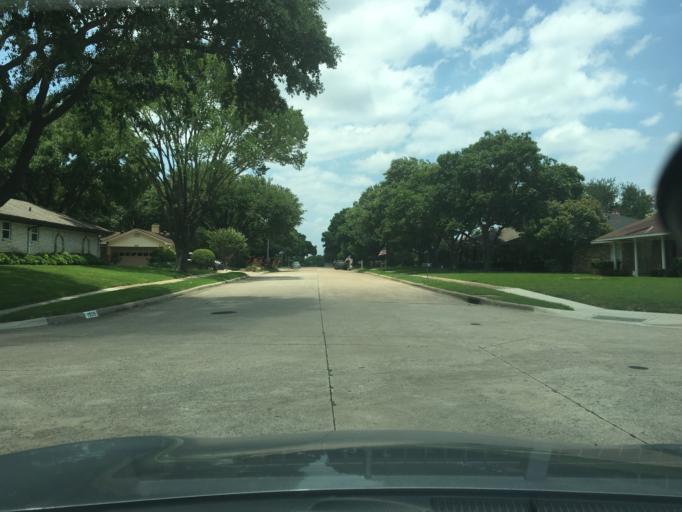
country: US
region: Texas
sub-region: Dallas County
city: Richardson
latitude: 32.9573
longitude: -96.6872
